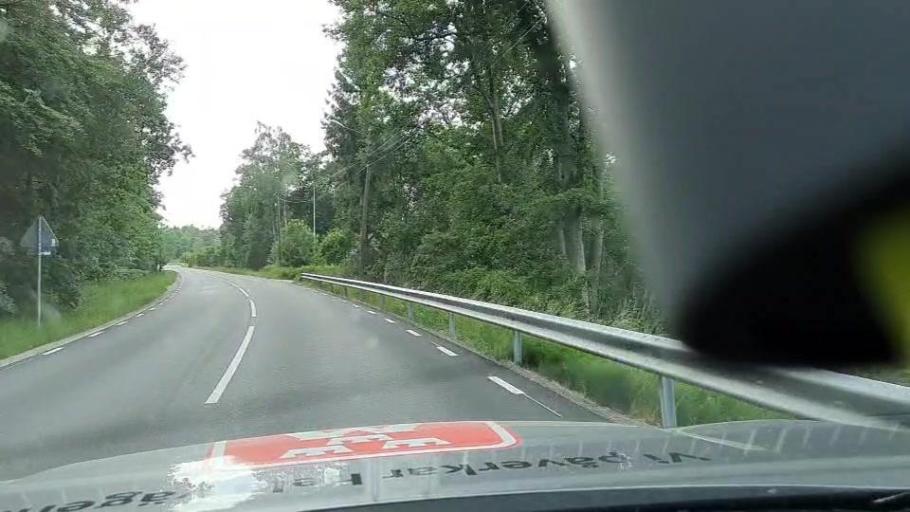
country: SE
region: Blekinge
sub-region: Ronneby Kommun
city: Brakne-Hoby
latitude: 56.2079
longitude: 14.9933
